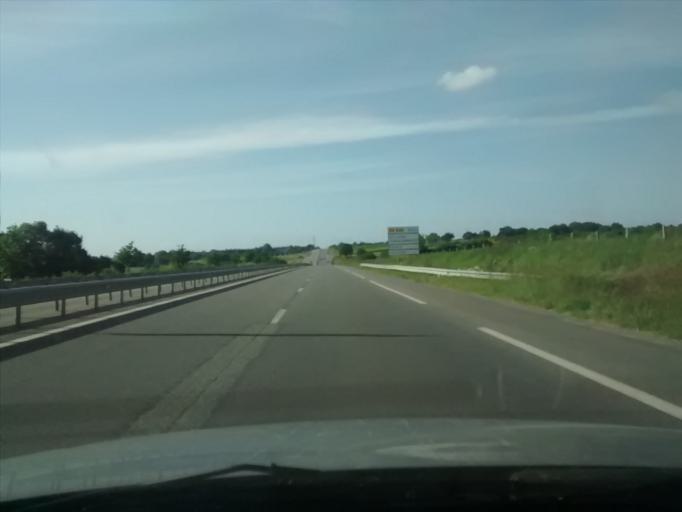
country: FR
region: Pays de la Loire
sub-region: Departement de la Mayenne
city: Chateau-Gontier
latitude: 47.9128
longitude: -0.6876
